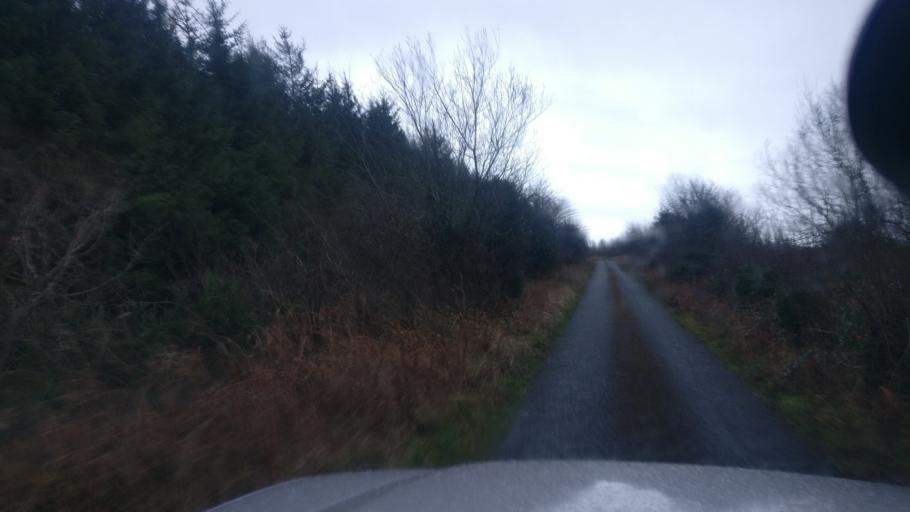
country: IE
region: Connaught
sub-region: County Galway
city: Loughrea
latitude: 53.2488
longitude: -8.4349
